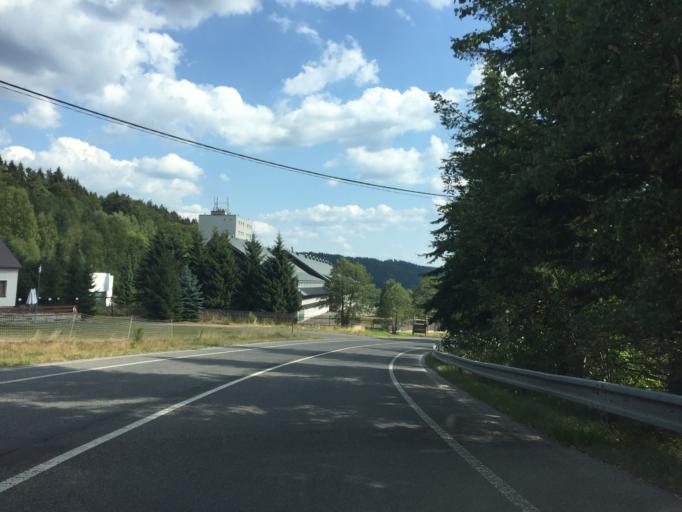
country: CZ
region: Liberecky
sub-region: Okres Jablonec nad Nisou
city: Janov nad Nisou
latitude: 50.7862
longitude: 15.1556
